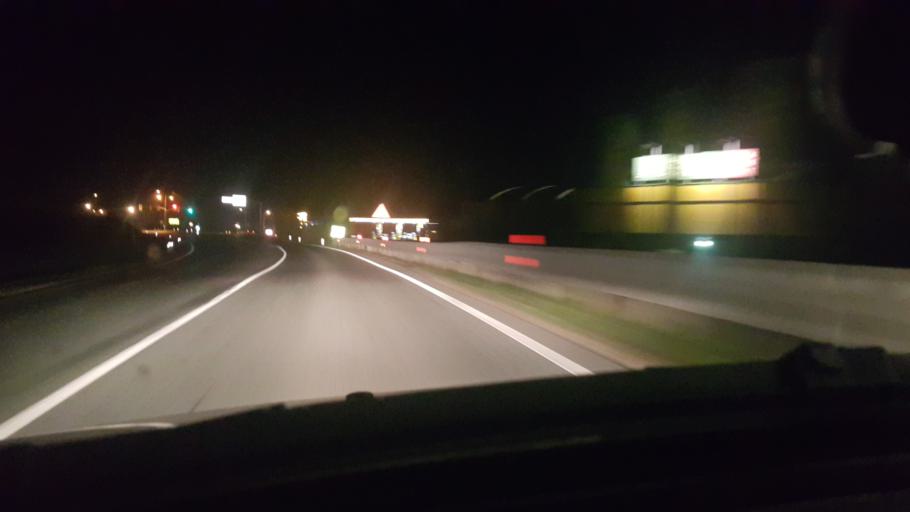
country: AT
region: Carinthia
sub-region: Politischer Bezirk Klagenfurt Land
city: Ebenthal
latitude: 46.6335
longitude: 14.3692
